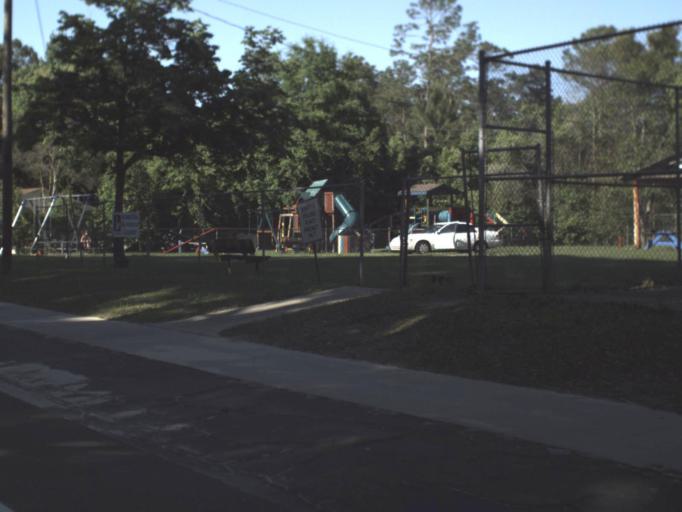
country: US
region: Florida
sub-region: Gulf County
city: Wewahitchka
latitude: 30.0208
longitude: -84.9797
